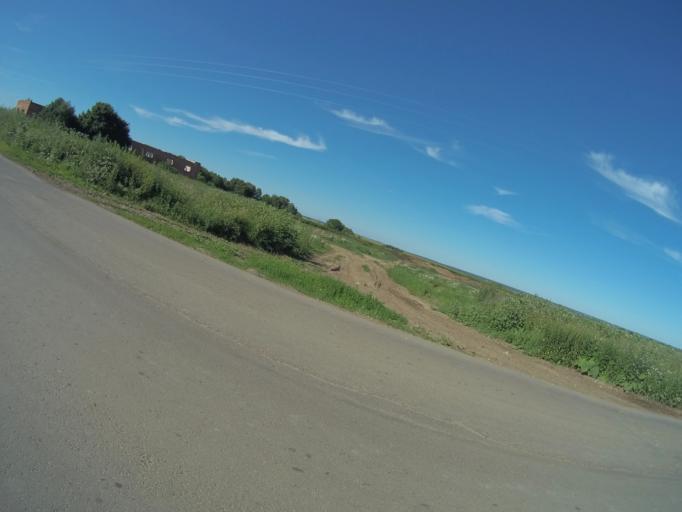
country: RU
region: Vladimir
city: Bogolyubovo
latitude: 56.2156
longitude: 40.4943
